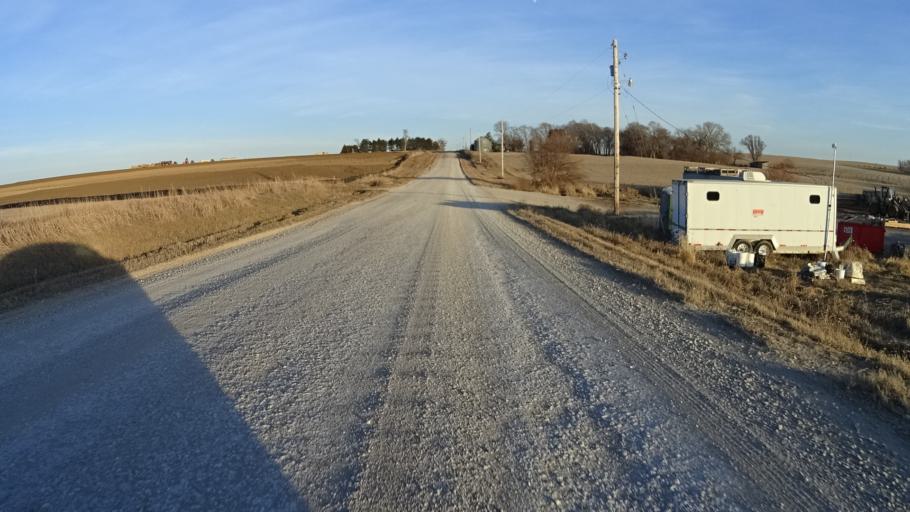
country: US
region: Nebraska
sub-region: Sarpy County
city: Springfield
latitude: 41.1326
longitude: -96.1109
